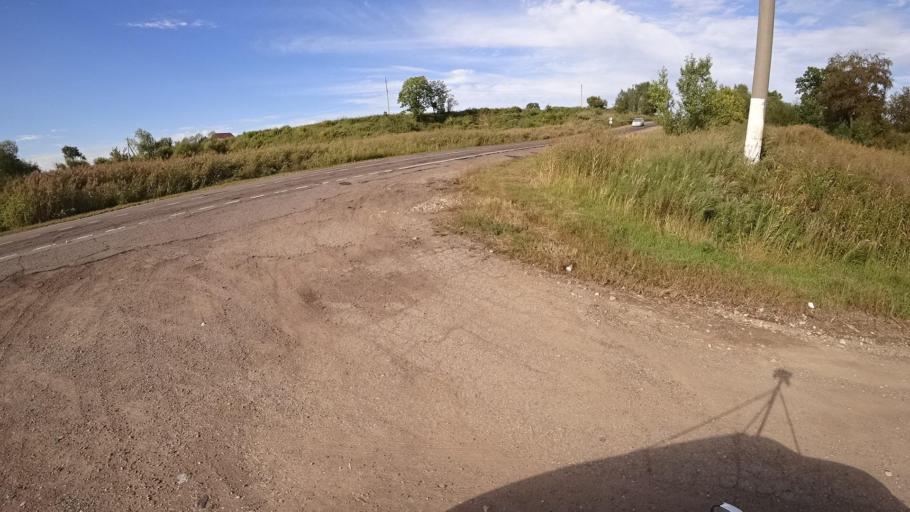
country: RU
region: Primorskiy
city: Dostoyevka
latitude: 44.3131
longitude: 133.4601
